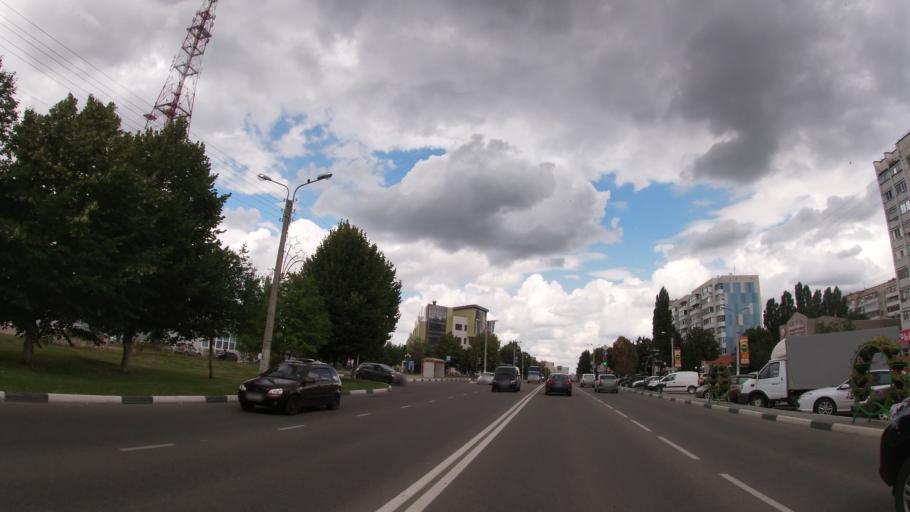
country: RU
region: Belgorod
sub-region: Belgorodskiy Rayon
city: Belgorod
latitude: 50.5746
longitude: 36.5832
